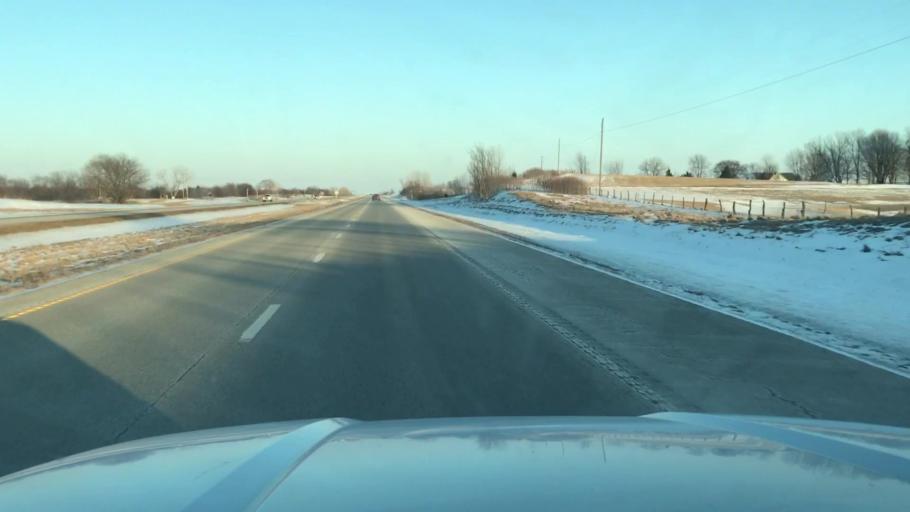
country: US
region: Missouri
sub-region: Clinton County
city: Gower
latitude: 39.7471
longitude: -94.6302
